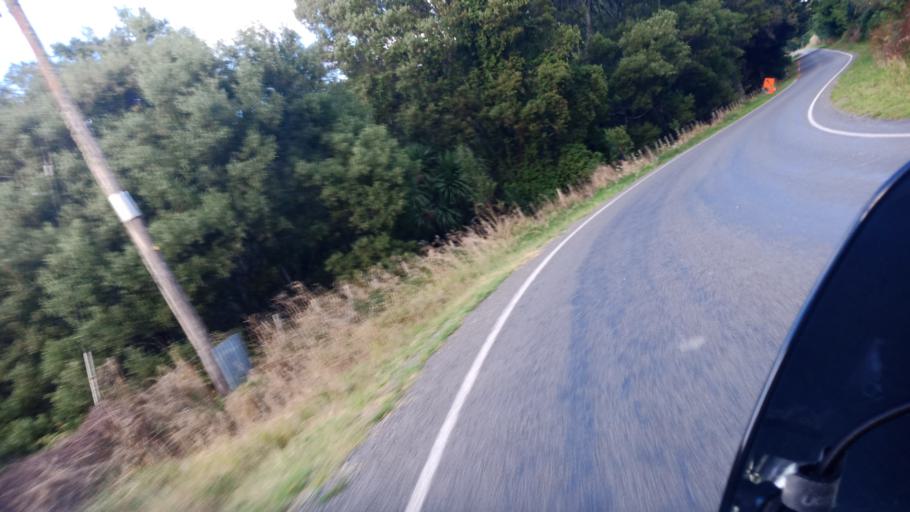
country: NZ
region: Gisborne
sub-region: Gisborne District
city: Gisborne
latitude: -38.5302
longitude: 177.5420
